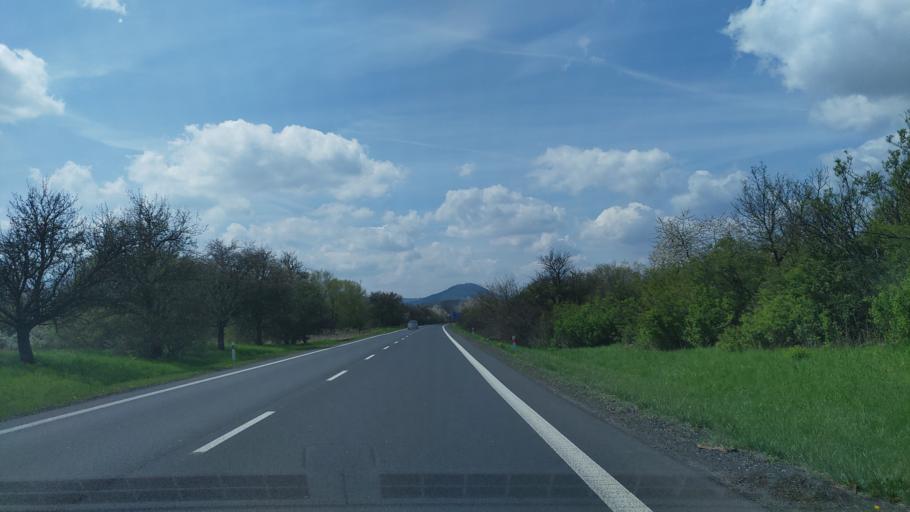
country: CZ
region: Ustecky
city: Kadan
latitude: 50.4086
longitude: 13.2423
